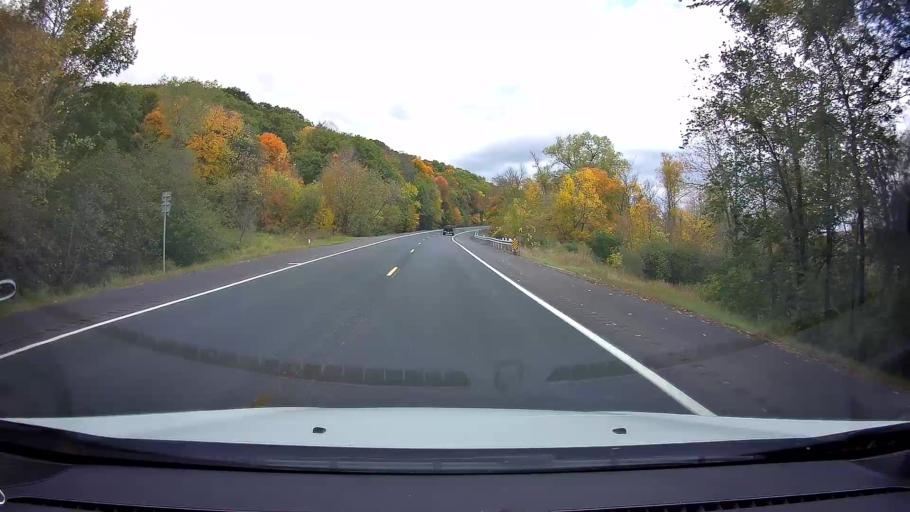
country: US
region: Wisconsin
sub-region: Polk County
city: Saint Croix Falls
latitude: 45.4115
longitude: -92.6537
